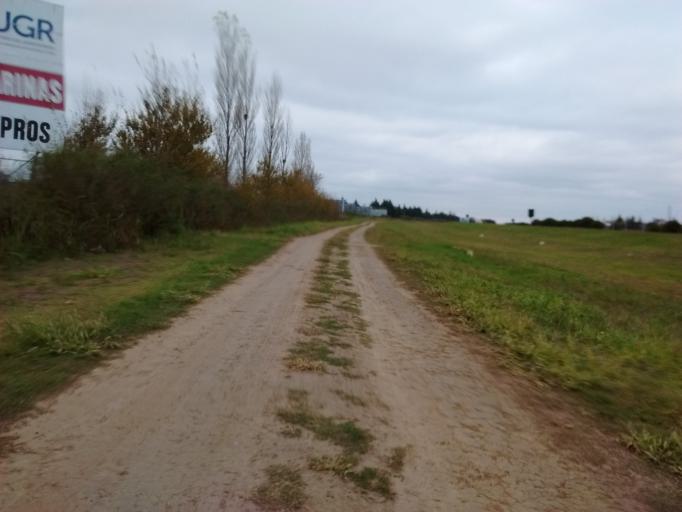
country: AR
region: Santa Fe
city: Funes
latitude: -32.9334
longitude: -60.8367
